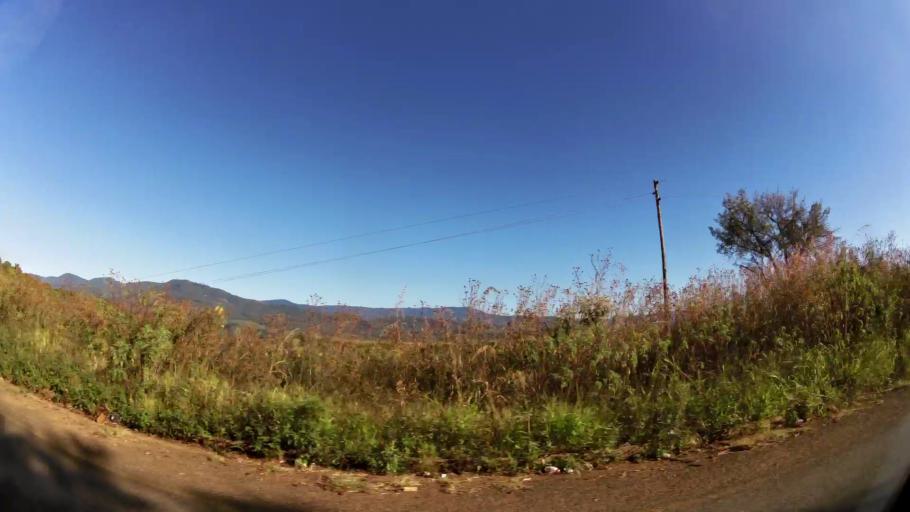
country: ZA
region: Limpopo
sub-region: Mopani District Municipality
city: Tzaneen
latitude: -23.8410
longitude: 30.1299
